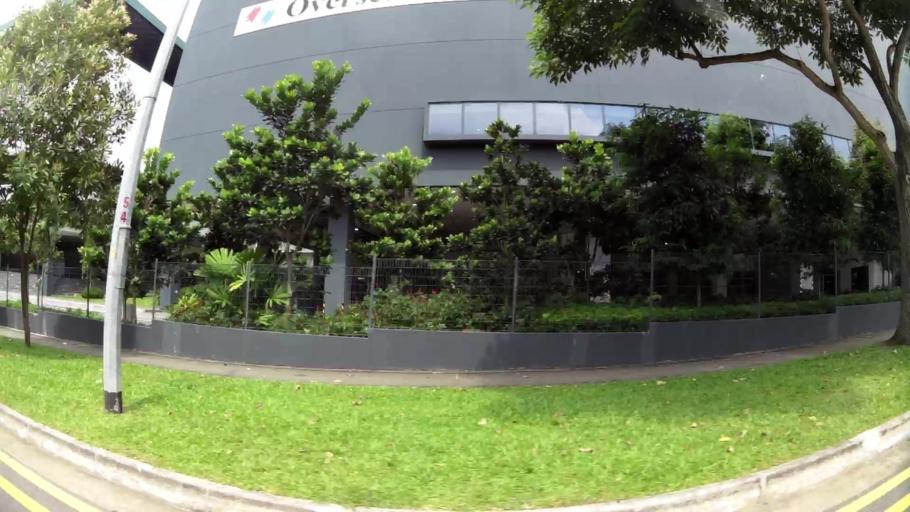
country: MY
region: Johor
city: Kampung Pasir Gudang Baru
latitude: 1.3803
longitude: 103.9425
